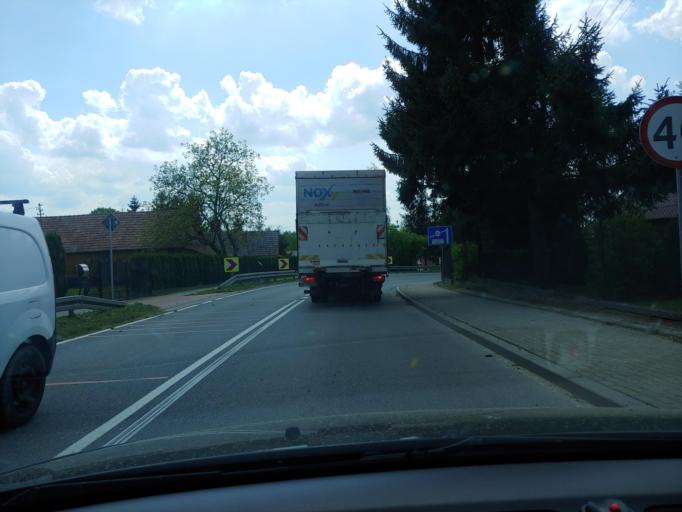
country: PL
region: Lesser Poland Voivodeship
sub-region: Powiat tarnowski
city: Lisia Gora
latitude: 50.0800
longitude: 21.0444
